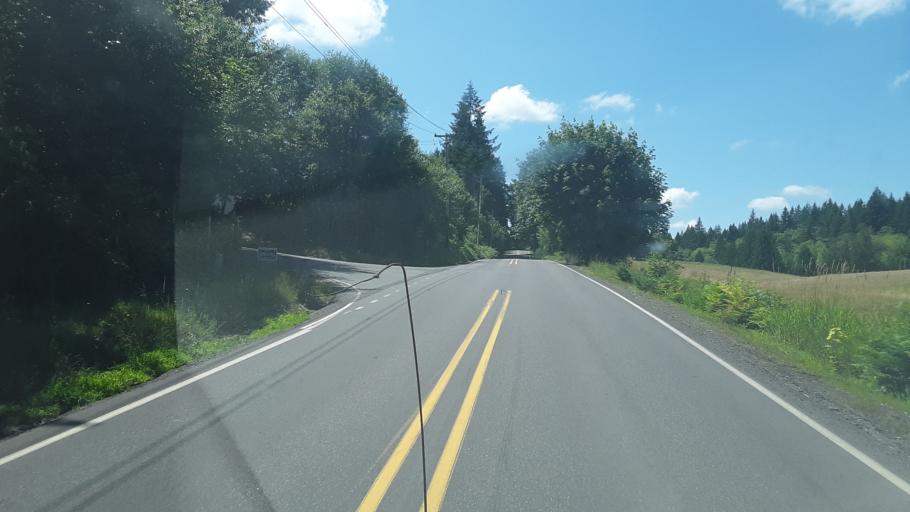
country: US
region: Washington
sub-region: Clark County
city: Amboy
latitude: 45.8958
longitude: -122.4623
